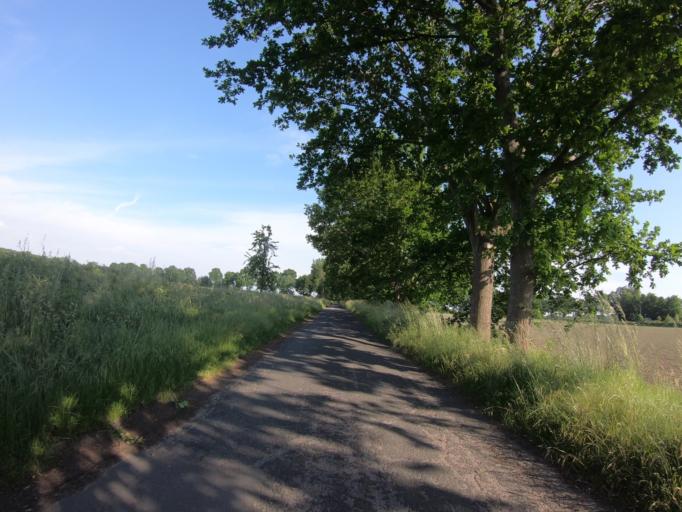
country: DE
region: Lower Saxony
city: Wasbuttel
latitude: 52.4132
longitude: 10.6045
